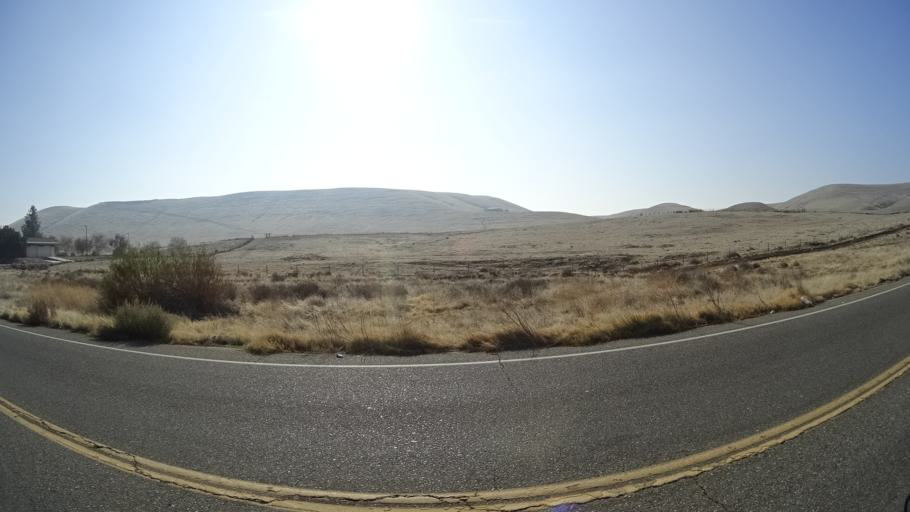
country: US
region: California
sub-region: Kern County
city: Oildale
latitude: 35.4304
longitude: -118.8727
